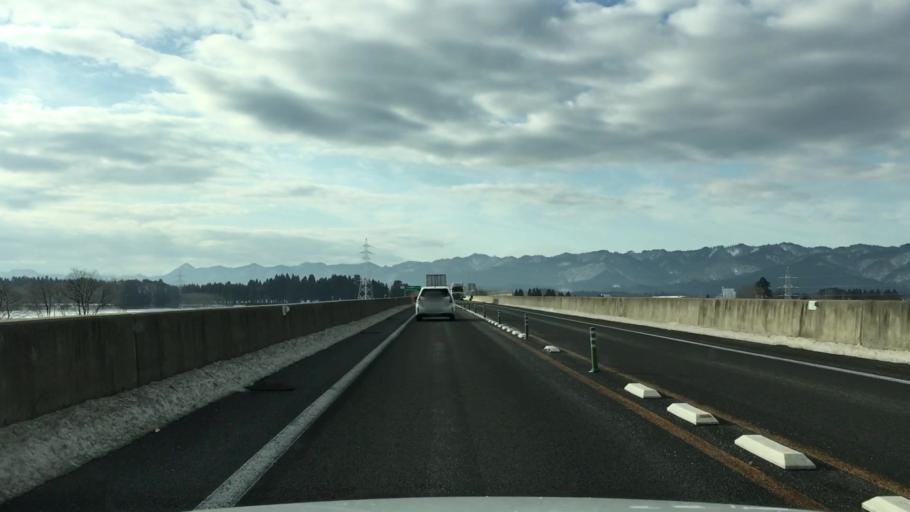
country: JP
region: Akita
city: Odate
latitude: 40.2655
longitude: 140.5263
